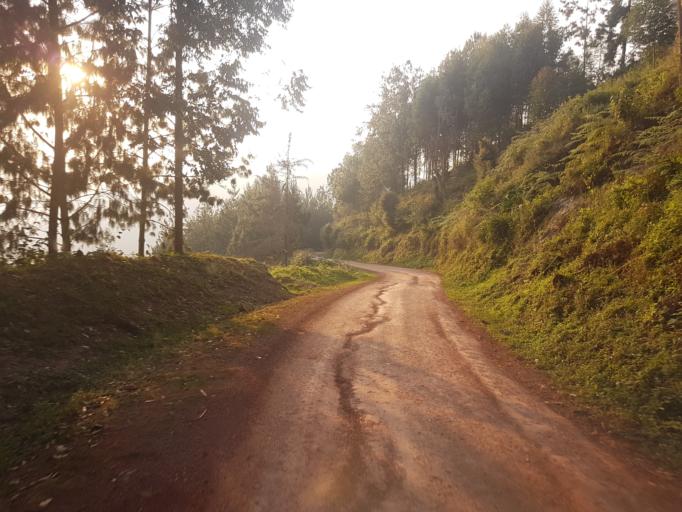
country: UG
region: Western Region
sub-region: Kanungu District
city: Kanungu
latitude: -1.0119
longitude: 29.8495
